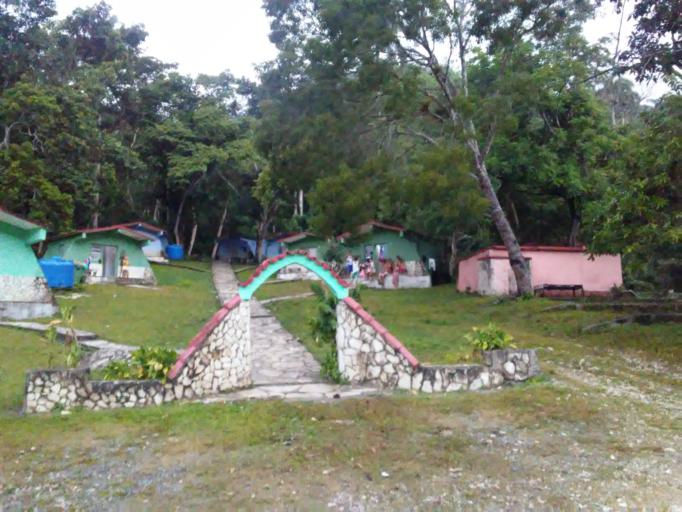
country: CU
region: Ciego de Avila
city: Florencia
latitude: 22.1720
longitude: -79.0240
